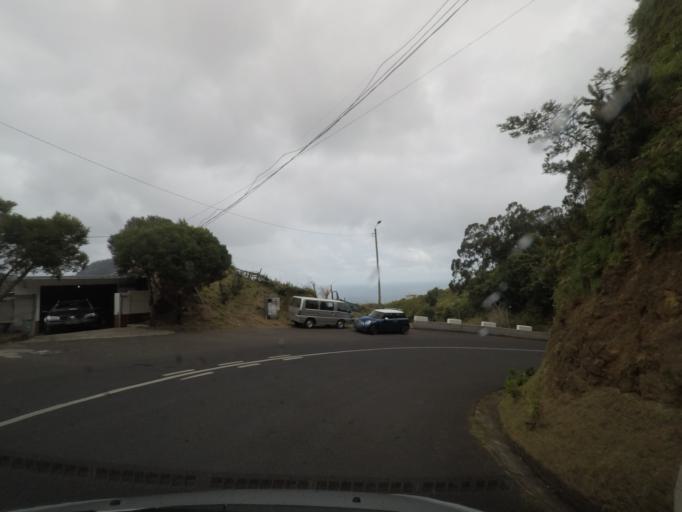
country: PT
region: Madeira
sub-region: Santana
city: Santana
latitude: 32.7516
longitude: -16.8394
